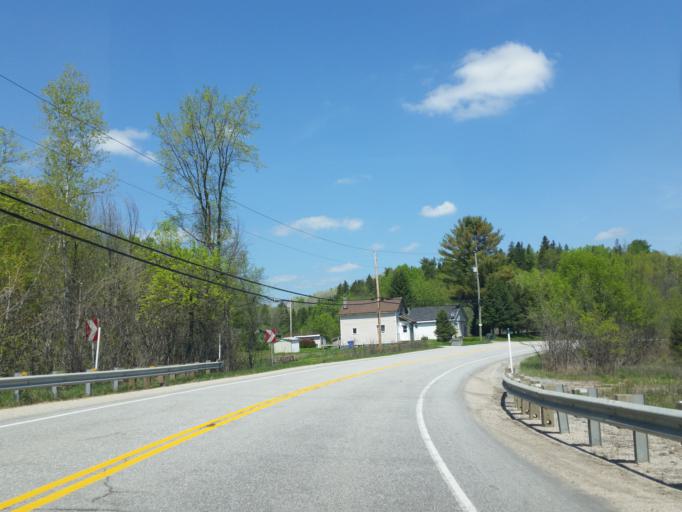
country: CA
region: Quebec
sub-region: Outaouais
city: Wakefield
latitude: 45.6572
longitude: -75.9289
